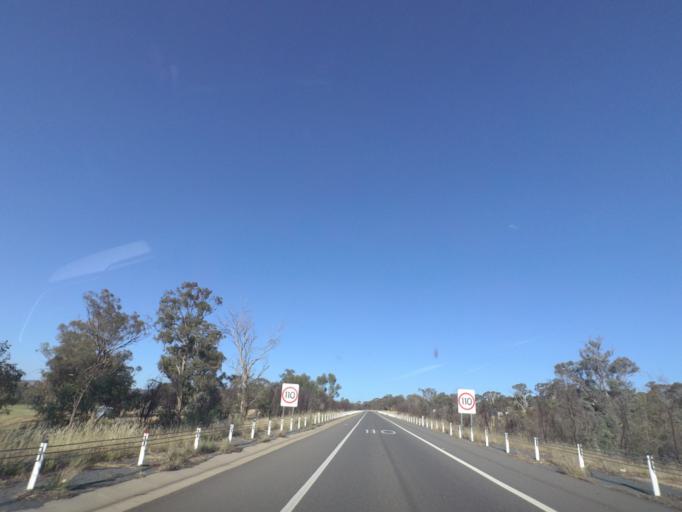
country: AU
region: New South Wales
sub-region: Wagga Wagga
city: Forest Hill
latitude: -35.2590
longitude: 147.7493
